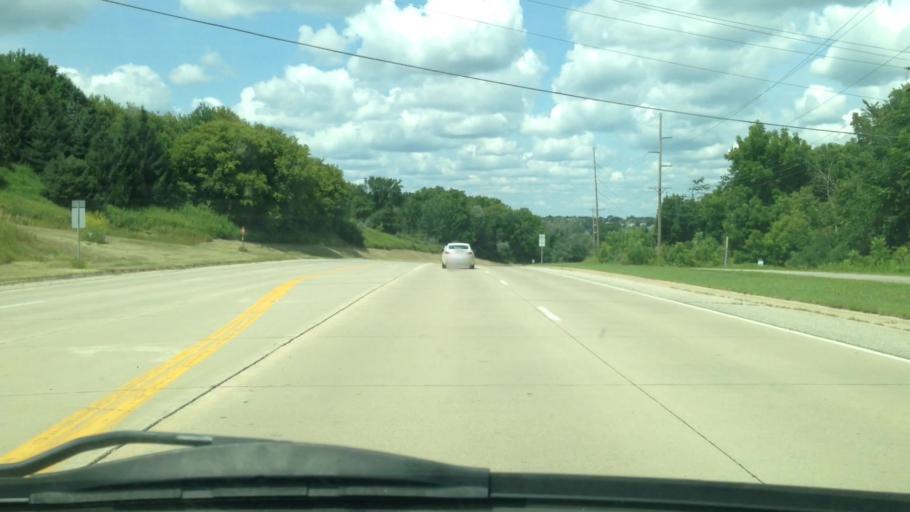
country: US
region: Minnesota
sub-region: Olmsted County
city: Rochester
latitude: 44.0129
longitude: -92.5134
